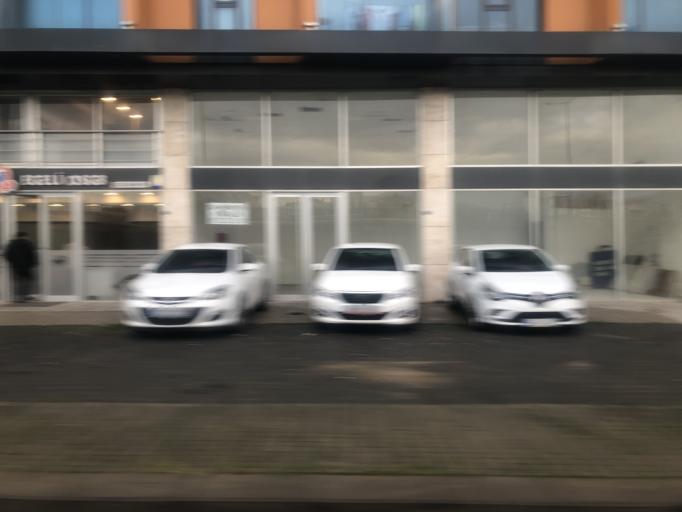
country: TR
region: Izmir
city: Bornova
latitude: 38.4506
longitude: 27.1905
